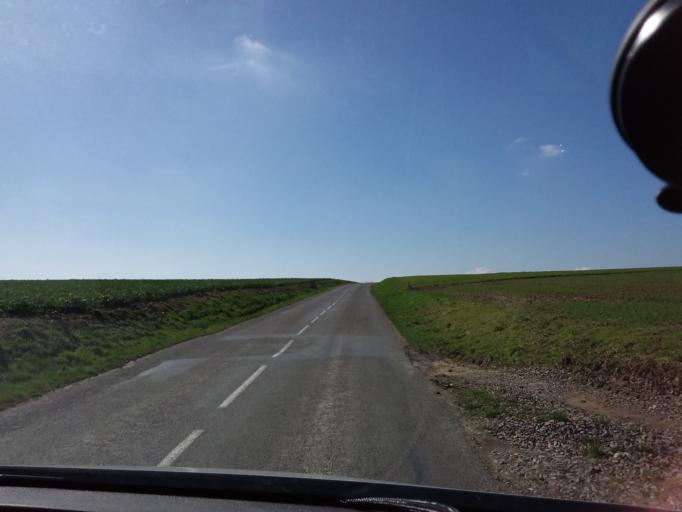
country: FR
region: Picardie
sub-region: Departement de l'Aisne
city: Montcornet
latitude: 49.7653
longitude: 4.0051
